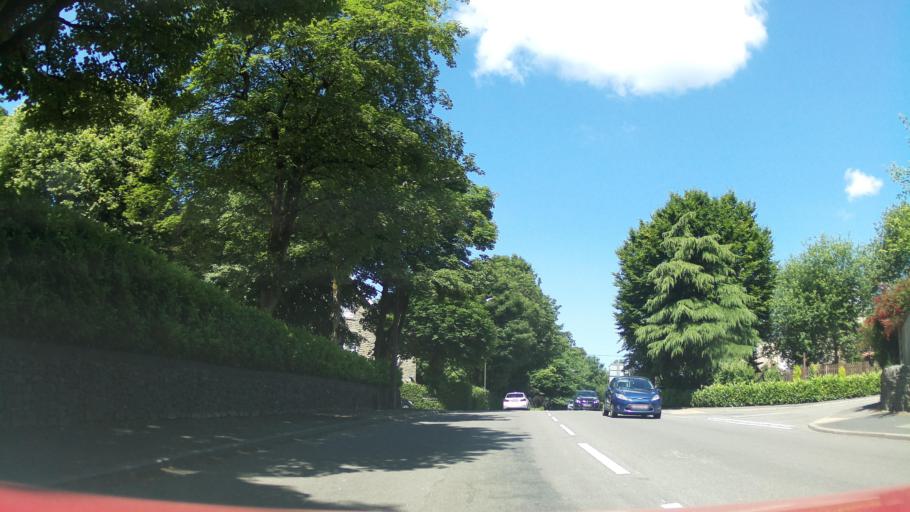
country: GB
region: England
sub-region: Derbyshire
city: Buxton
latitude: 53.2484
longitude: -1.9098
